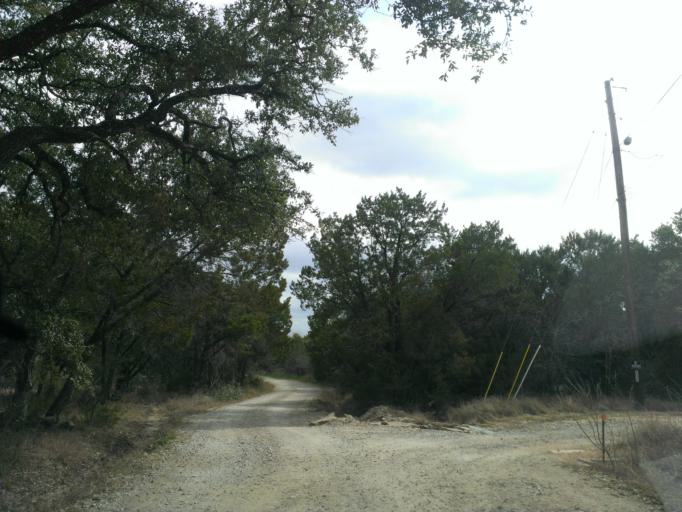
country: US
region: Texas
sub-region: Travis County
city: Briarcliff
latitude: 30.3916
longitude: -98.0984
